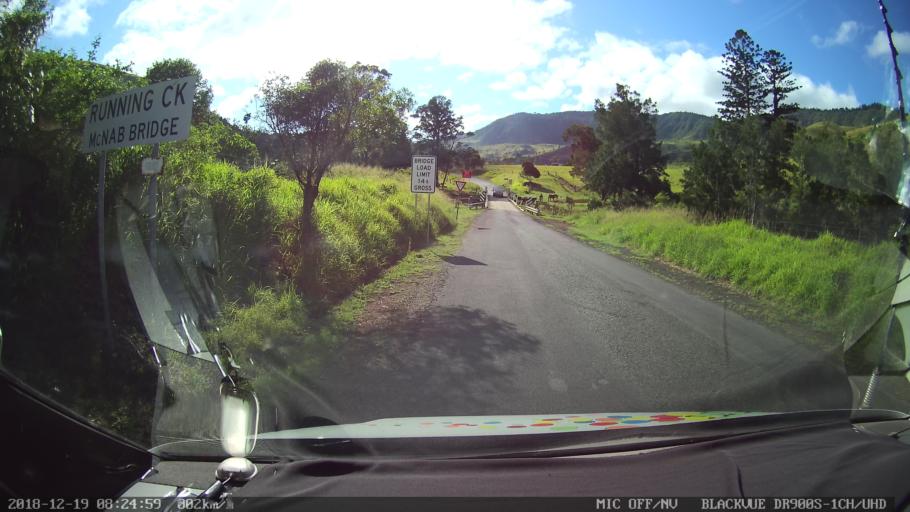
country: AU
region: New South Wales
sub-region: Kyogle
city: Kyogle
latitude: -28.3137
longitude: 152.9155
